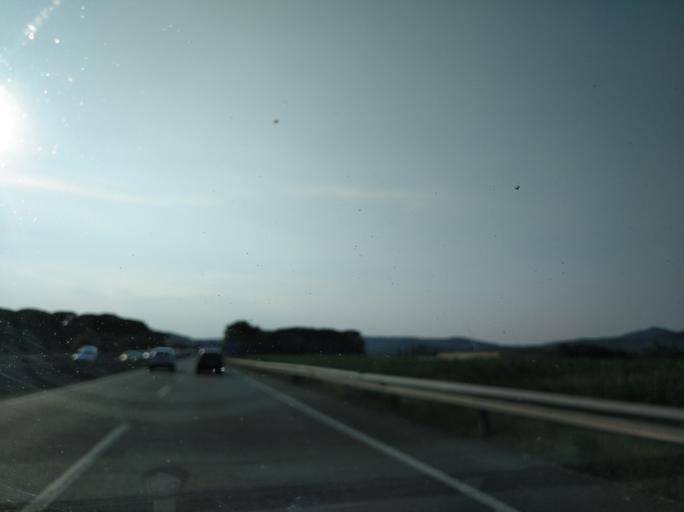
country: ES
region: Catalonia
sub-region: Provincia de Girona
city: Santa Cristina d'Aro
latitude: 41.8159
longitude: 2.9855
